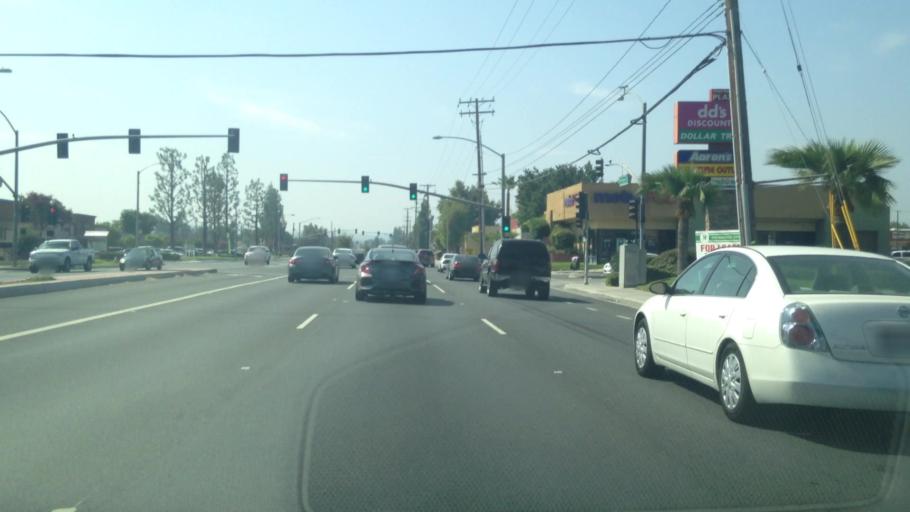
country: US
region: California
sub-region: Riverside County
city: Pedley
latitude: 33.9415
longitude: -117.4541
